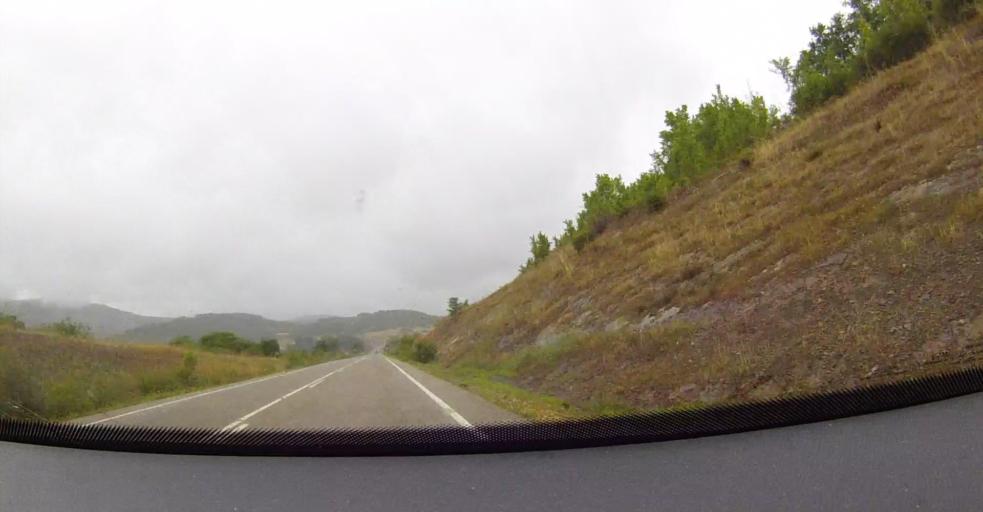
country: ES
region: Castille and Leon
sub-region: Provincia de Leon
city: Bonar
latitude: 42.8389
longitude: -5.2399
